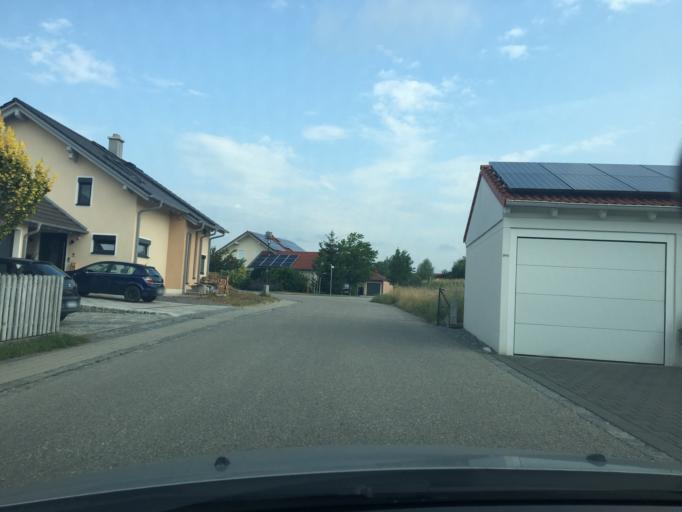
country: DE
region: Bavaria
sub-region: Upper Bavaria
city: Neumarkt-Sankt Veit
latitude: 48.3620
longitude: 12.5010
